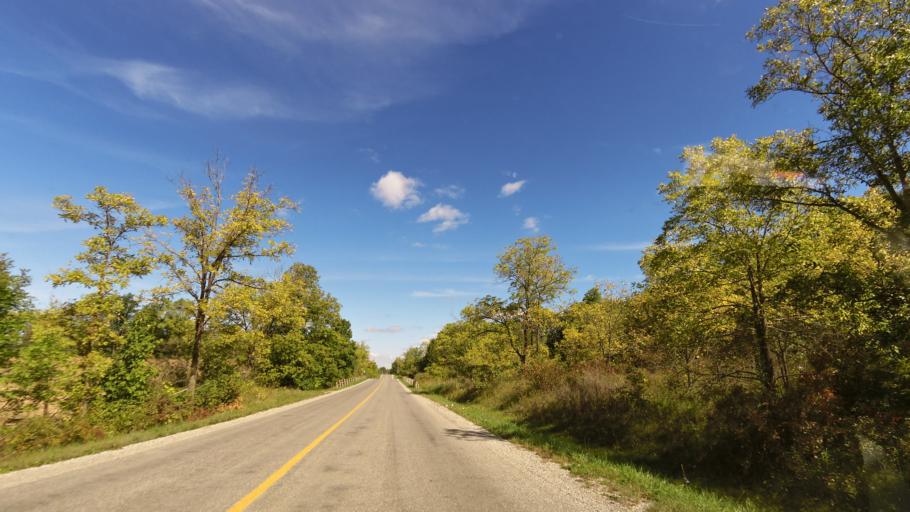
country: CA
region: Ontario
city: Brantford
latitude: 43.0886
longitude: -80.1387
